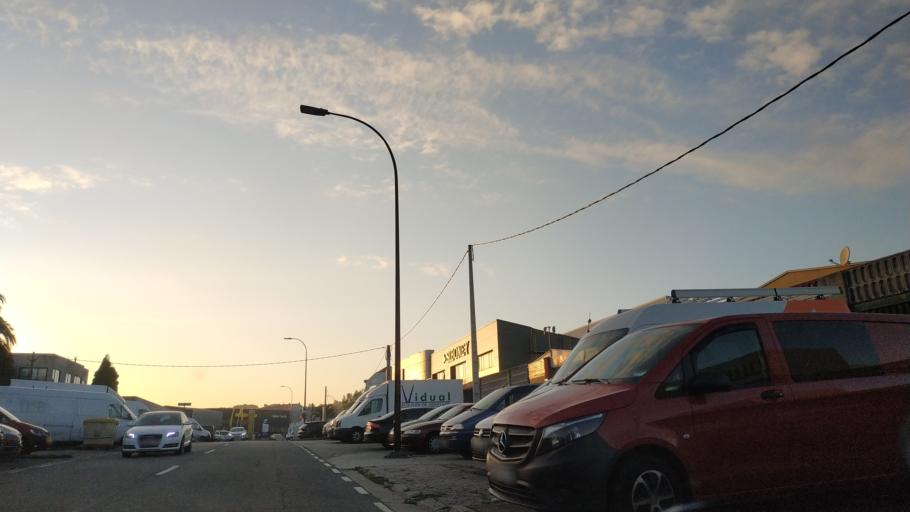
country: ES
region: Galicia
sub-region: Provincia da Coruna
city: A Coruna
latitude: 43.3562
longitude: -8.4196
